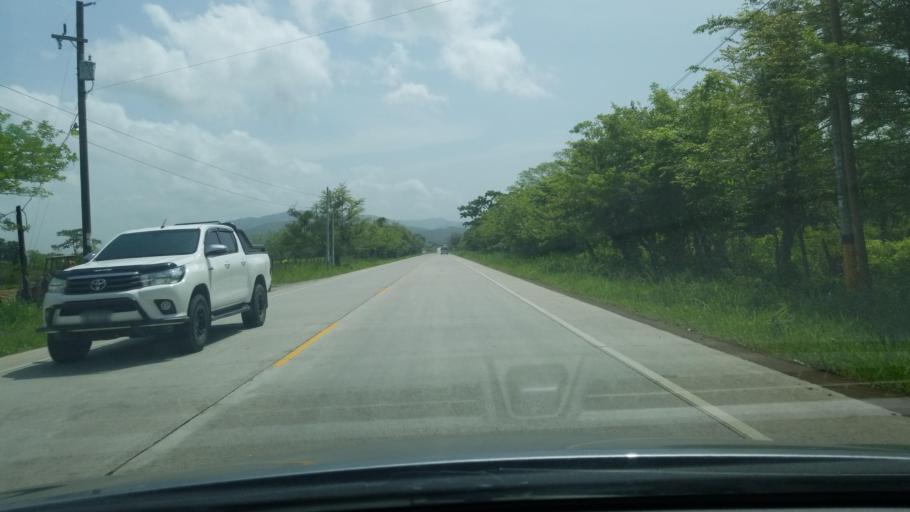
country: HN
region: Copan
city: Florida
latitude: 15.0511
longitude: -88.8014
